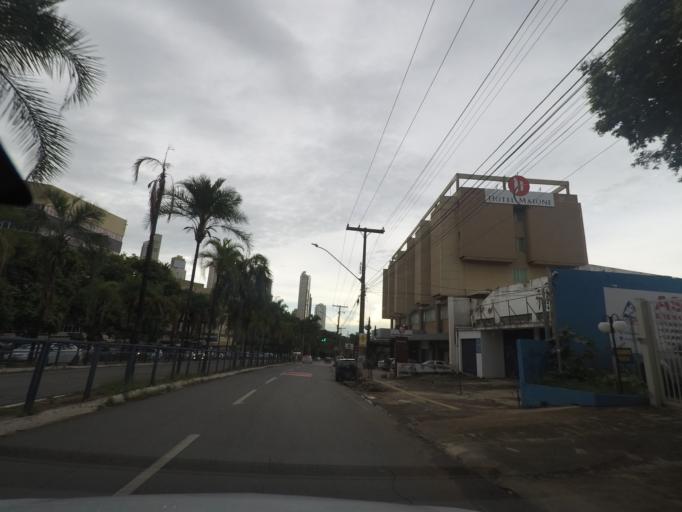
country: BR
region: Goias
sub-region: Goiania
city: Goiania
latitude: -16.7084
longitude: -49.2544
